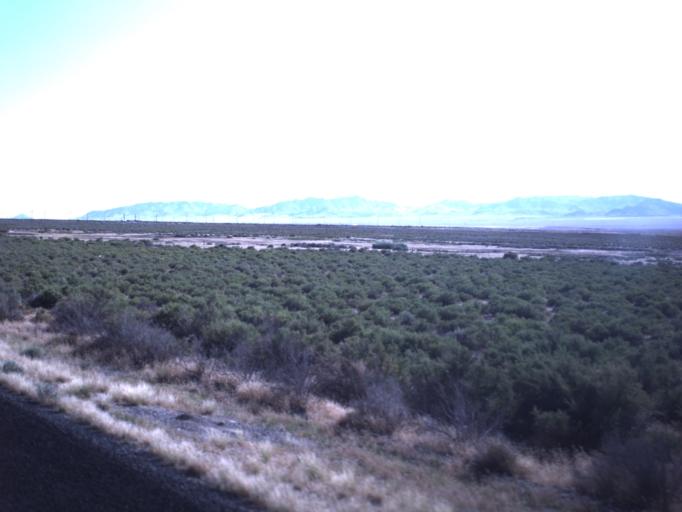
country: US
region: Utah
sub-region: Beaver County
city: Milford
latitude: 38.4520
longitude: -113.0069
